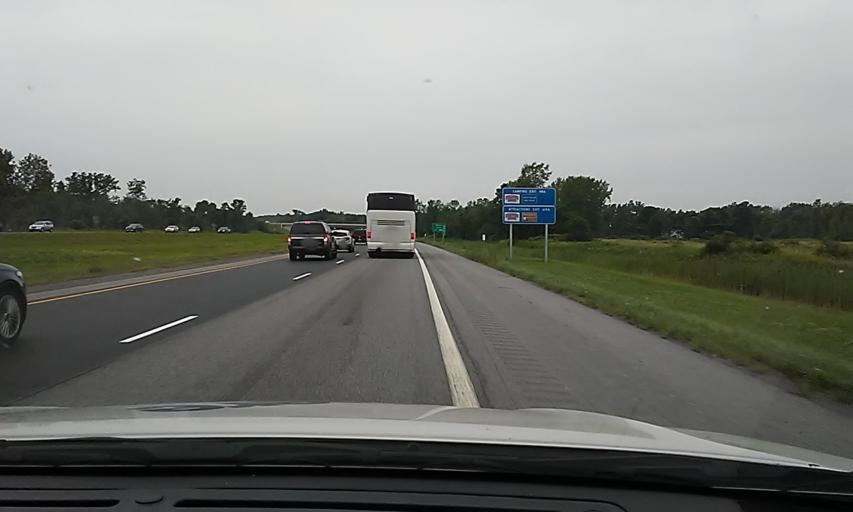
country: US
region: New York
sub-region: Erie County
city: Akron
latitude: 43.0093
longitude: -78.3991
